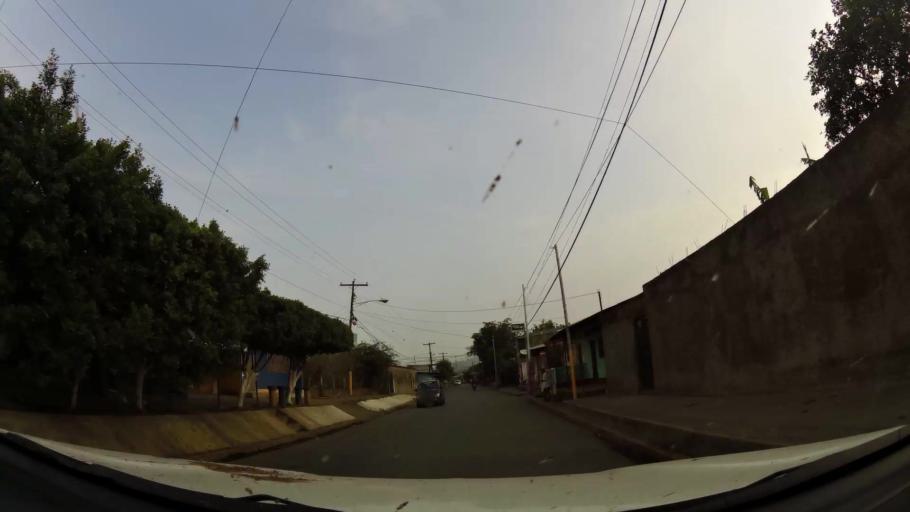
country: NI
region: Masaya
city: Masaya
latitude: 11.9810
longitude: -86.1015
